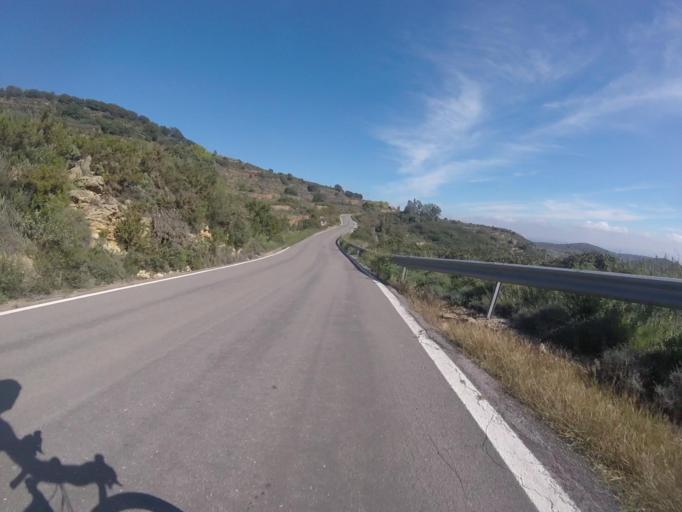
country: ES
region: Valencia
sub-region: Provincia de Castello
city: Sarratella
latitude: 40.3173
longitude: 0.0254
